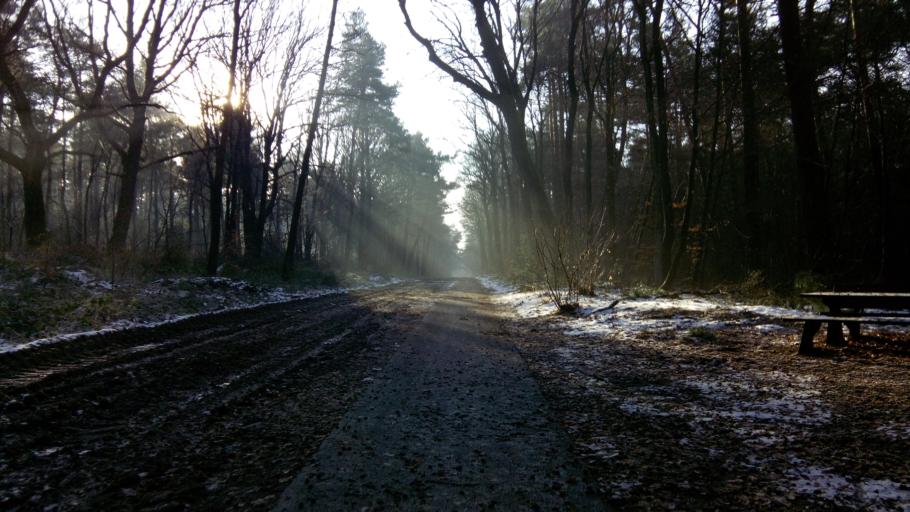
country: NL
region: Gelderland
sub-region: Gemeente Groesbeek
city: Berg en Dal
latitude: 51.8065
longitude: 5.8799
